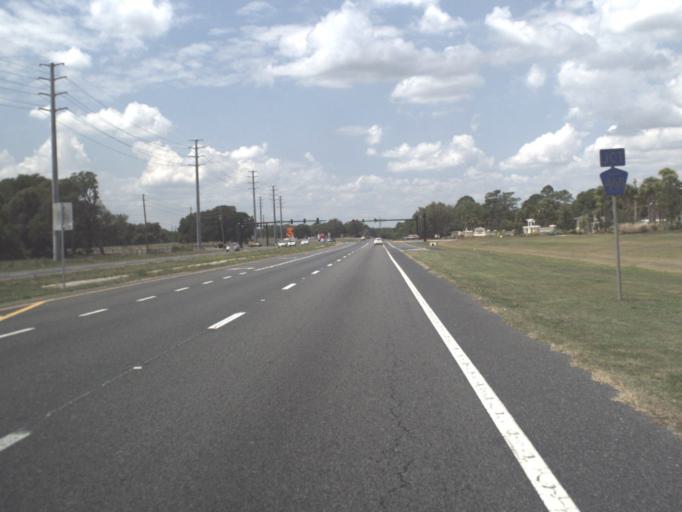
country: US
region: Florida
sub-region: Lake County
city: Fruitland Park
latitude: 28.8238
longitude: -81.9713
